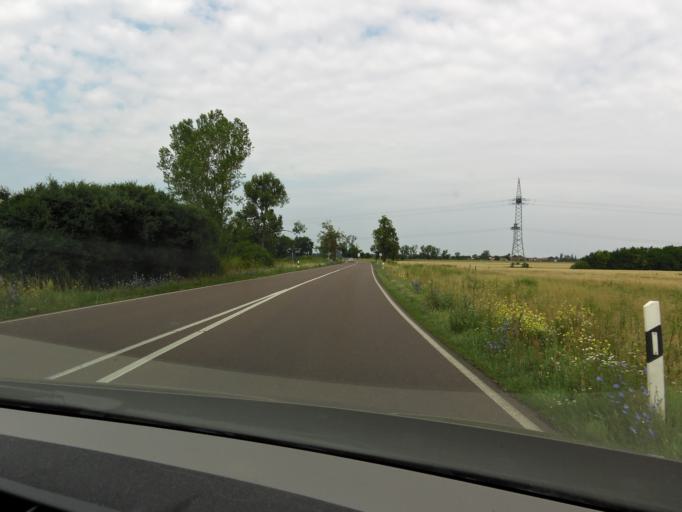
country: DE
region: Saxony-Anhalt
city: Kemberg
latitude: 51.8076
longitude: 12.6489
